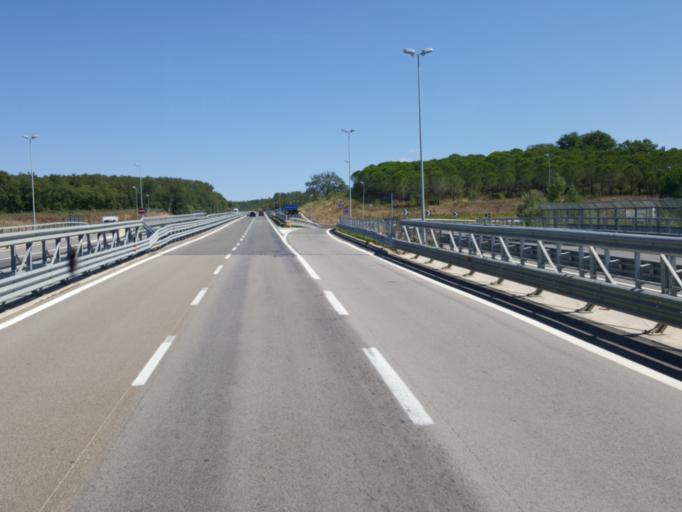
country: IT
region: Tuscany
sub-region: Provincia di Grosseto
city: Civitella Marittima
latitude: 42.9412
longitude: 11.2740
